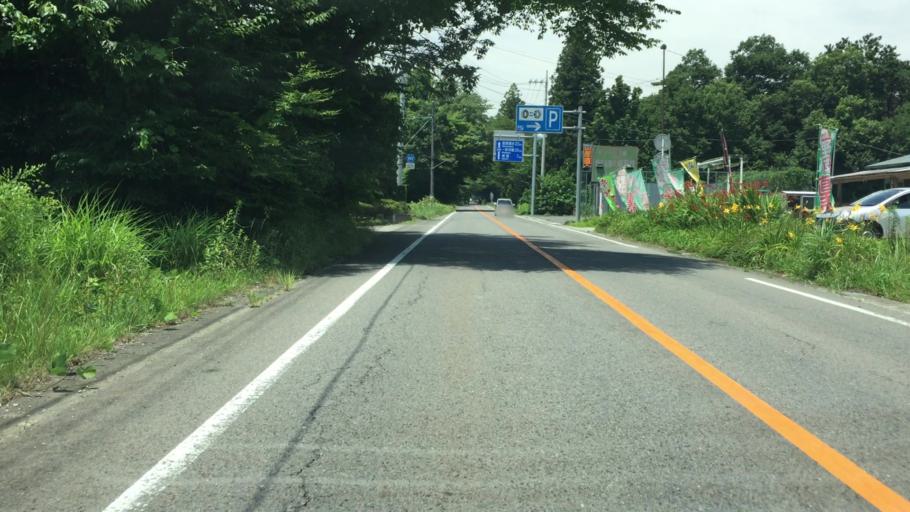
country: JP
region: Tochigi
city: Kuroiso
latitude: 37.0143
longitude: 139.9604
